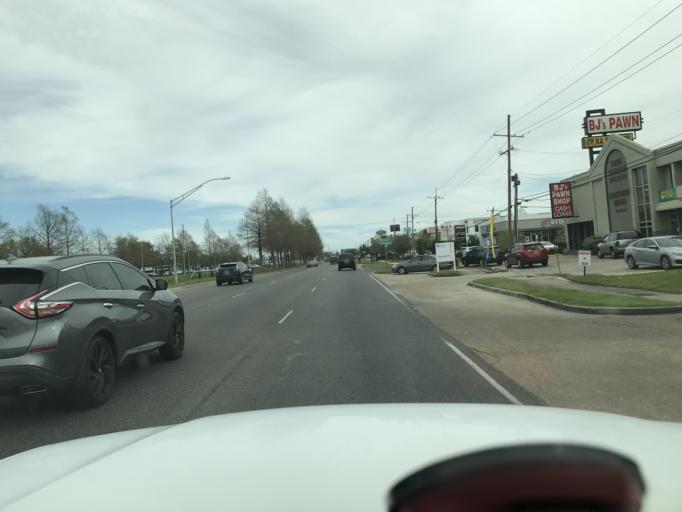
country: US
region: Louisiana
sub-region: Jefferson Parish
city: Metairie Terrace
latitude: 30.0039
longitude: -90.1700
